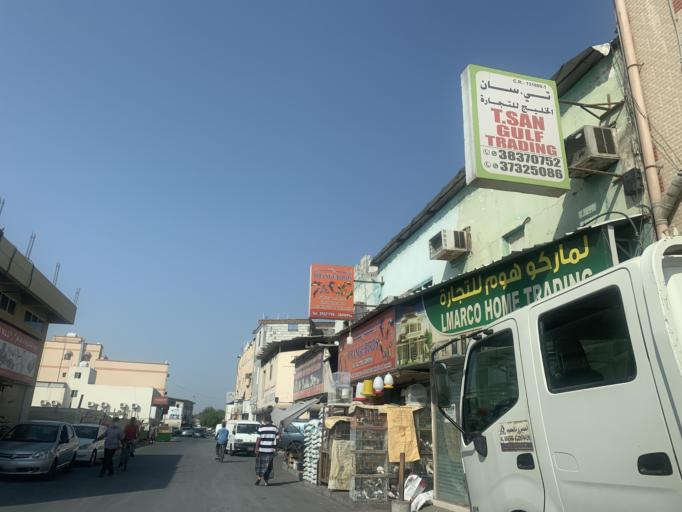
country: BH
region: Central Governorate
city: Madinat Hamad
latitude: 26.1422
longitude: 50.4936
